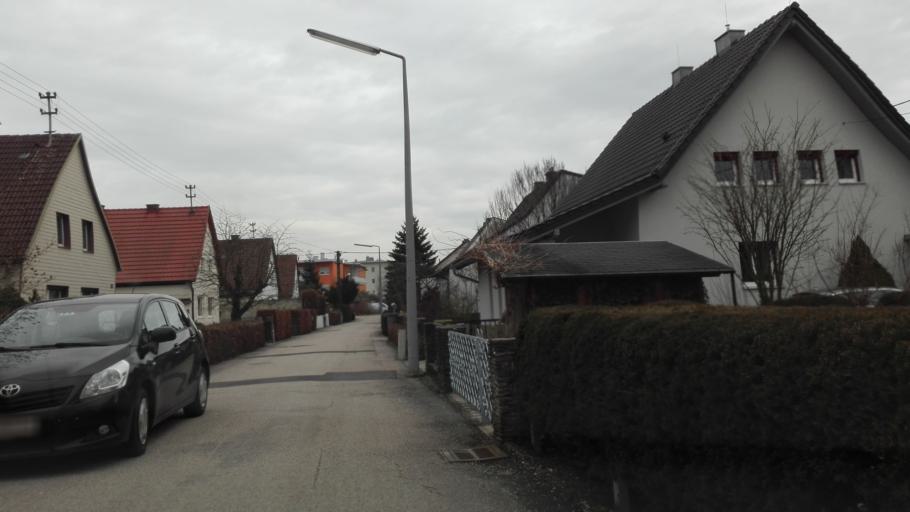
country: AT
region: Upper Austria
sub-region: Politischer Bezirk Linz-Land
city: Traun
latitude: 48.2456
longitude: 14.2556
